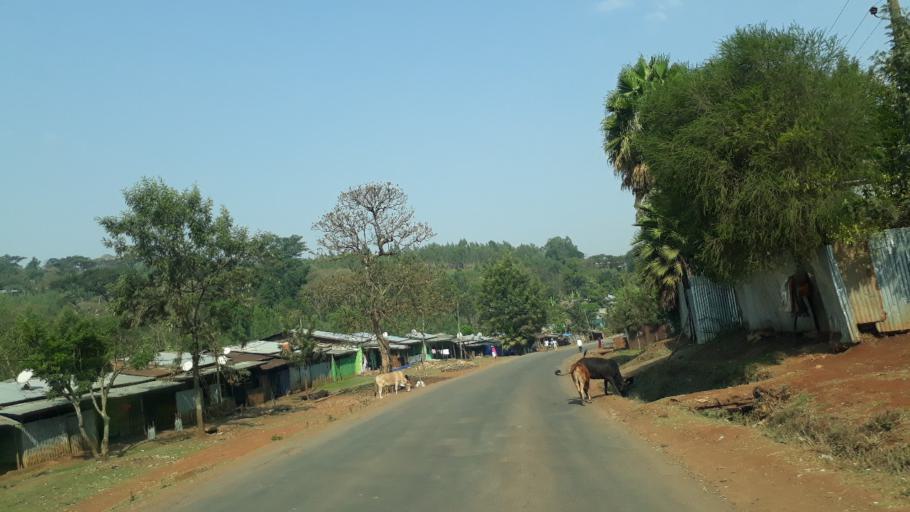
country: ET
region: Oromiya
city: Agaro
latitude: 7.8382
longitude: 36.6662
